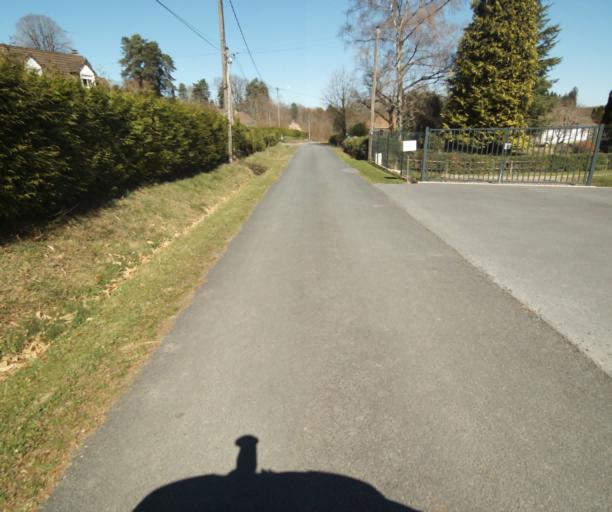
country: FR
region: Limousin
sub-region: Departement de la Correze
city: Saint-Mexant
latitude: 45.2752
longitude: 1.6712
